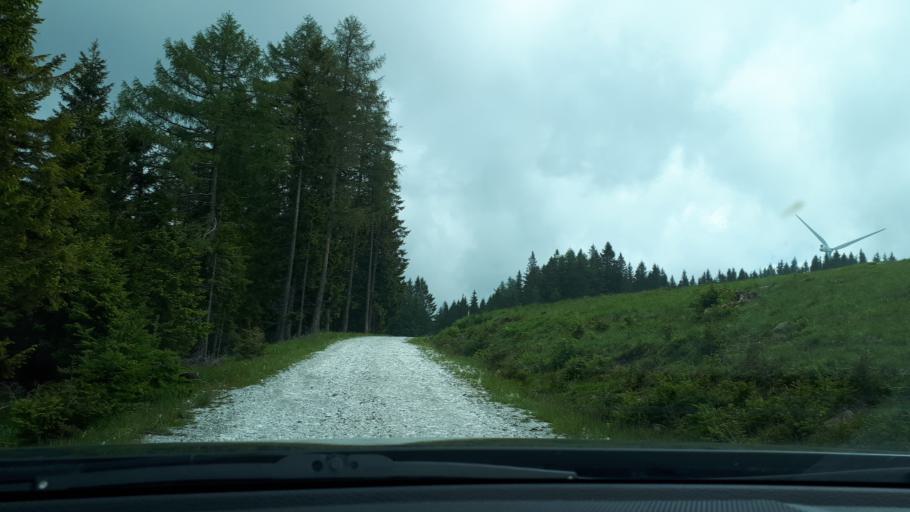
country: AT
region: Styria
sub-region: Politischer Bezirk Voitsberg
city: Modriach
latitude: 46.9100
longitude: 15.0468
